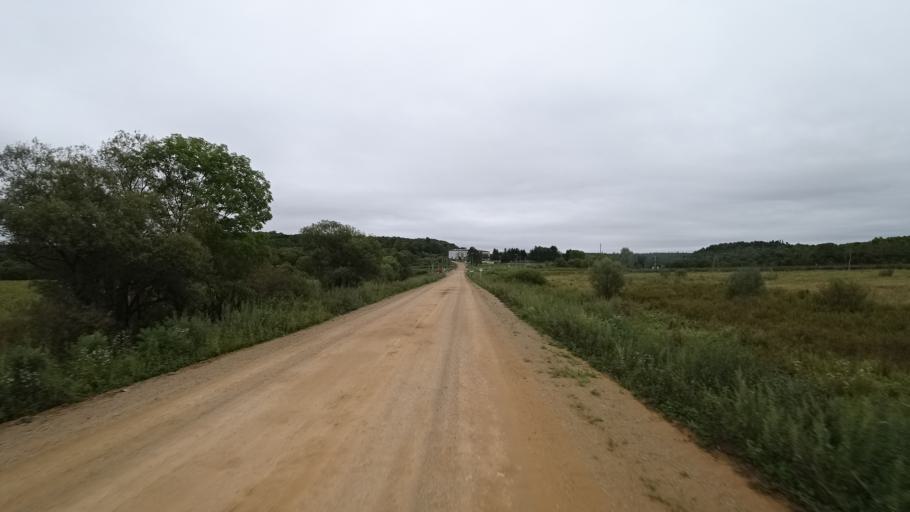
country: RU
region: Primorskiy
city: Rettikhovka
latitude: 44.1755
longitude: 132.8773
